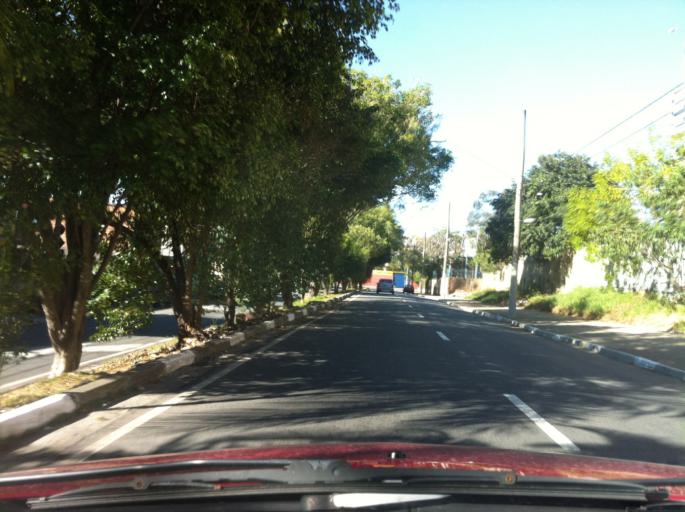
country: BR
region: Sao Paulo
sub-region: Ferraz De Vasconcelos
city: Ferraz de Vasconcelos
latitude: -23.5494
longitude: -46.4276
